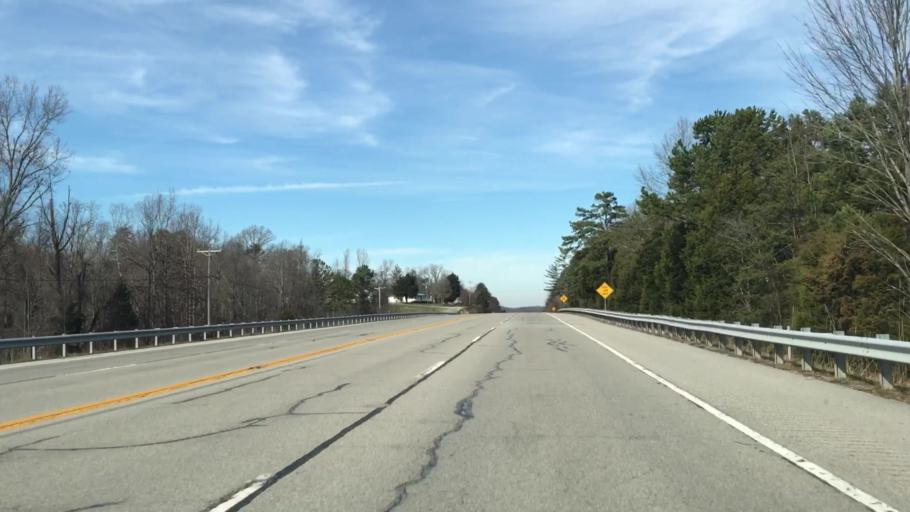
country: US
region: Kentucky
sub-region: Pulaski County
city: Somerset
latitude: 36.9234
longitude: -84.5197
